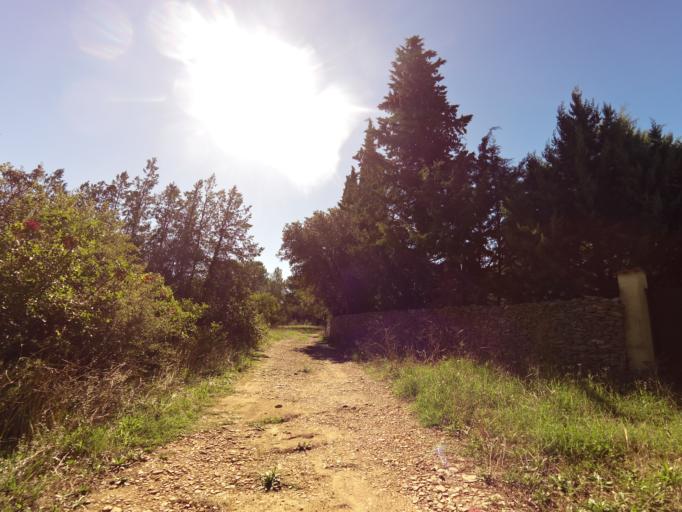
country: FR
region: Languedoc-Roussillon
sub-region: Departement de l'Herault
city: Villetelle
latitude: 43.7435
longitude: 4.1313
